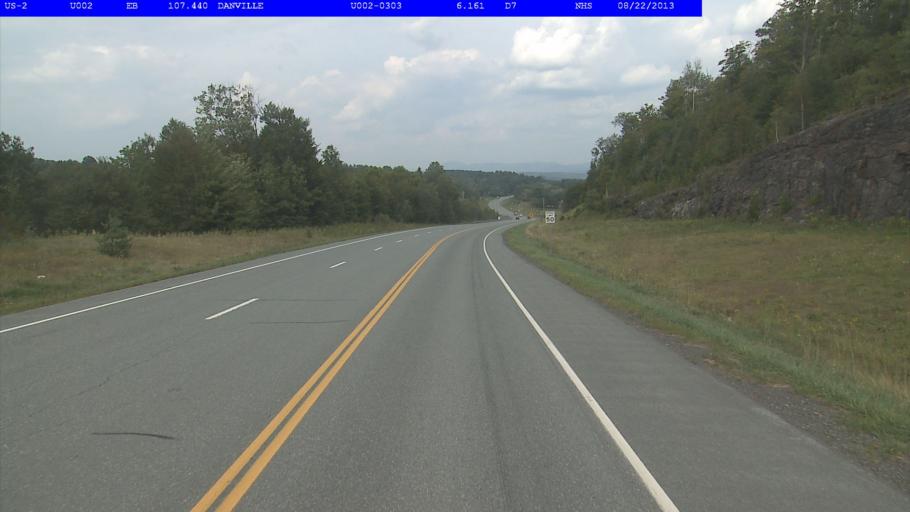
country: US
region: Vermont
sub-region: Caledonia County
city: St Johnsbury
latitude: 44.4248
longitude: -72.1117
